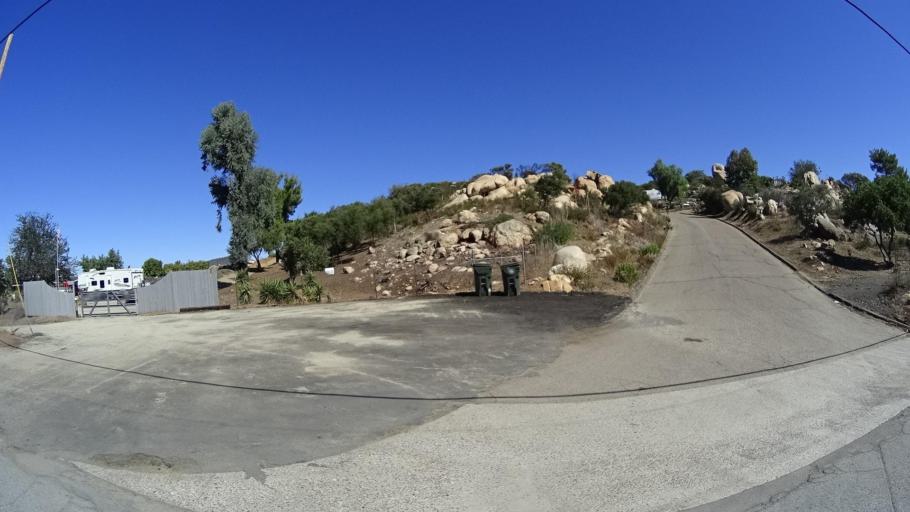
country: US
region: California
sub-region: San Diego County
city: Alpine
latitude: 32.7254
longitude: -116.7644
